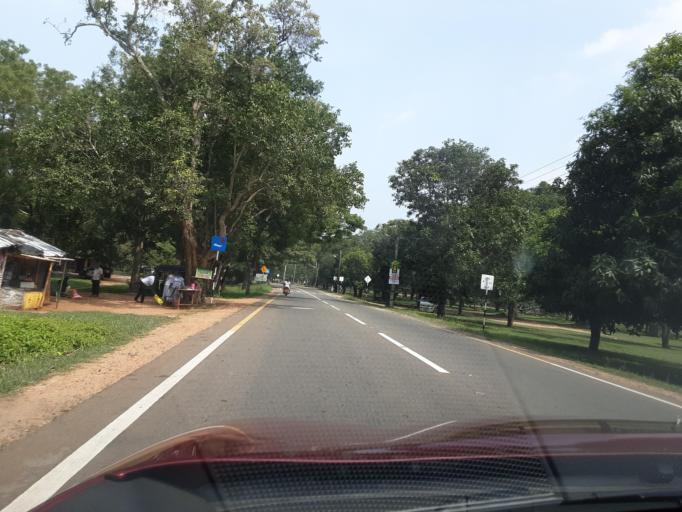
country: LK
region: North Central
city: Anuradhapura
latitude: 8.3548
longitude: 80.5100
